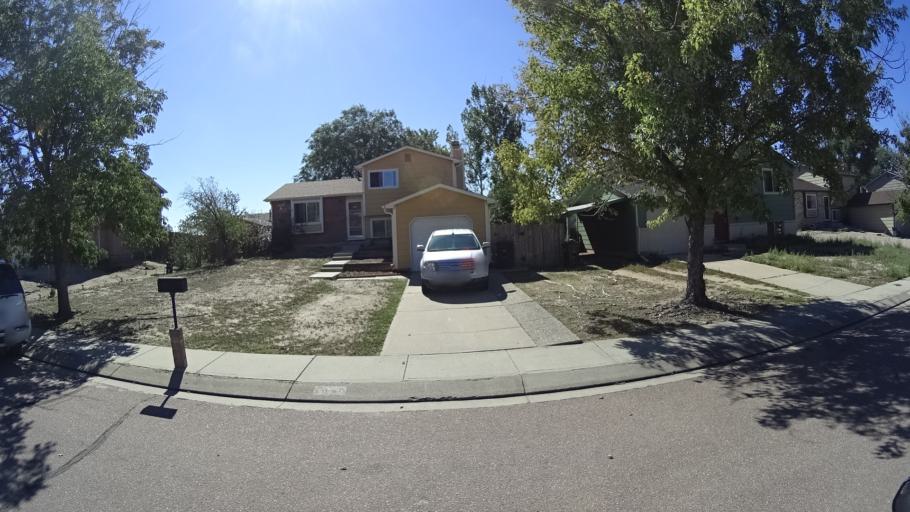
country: US
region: Colorado
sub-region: El Paso County
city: Cimarron Hills
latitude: 38.8176
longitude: -104.7334
